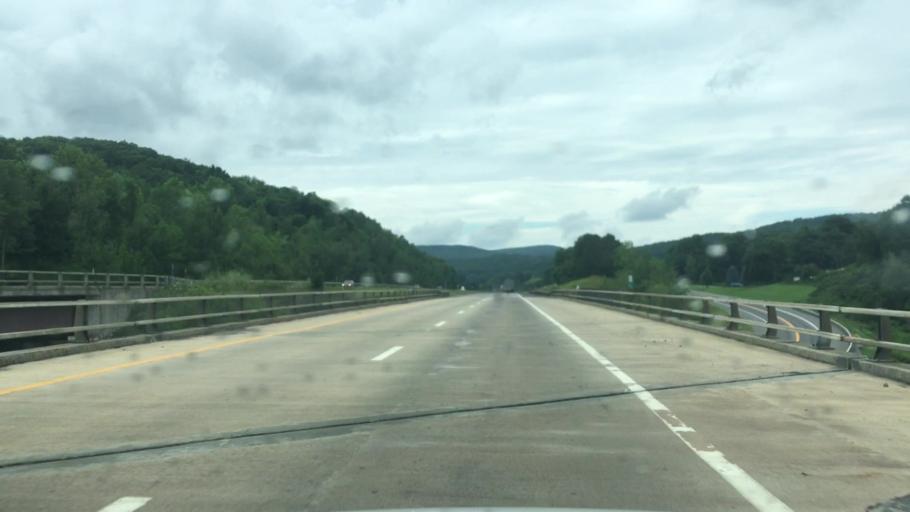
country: US
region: New York
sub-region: Schoharie County
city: Cobleskill
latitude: 42.6447
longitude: -74.5887
